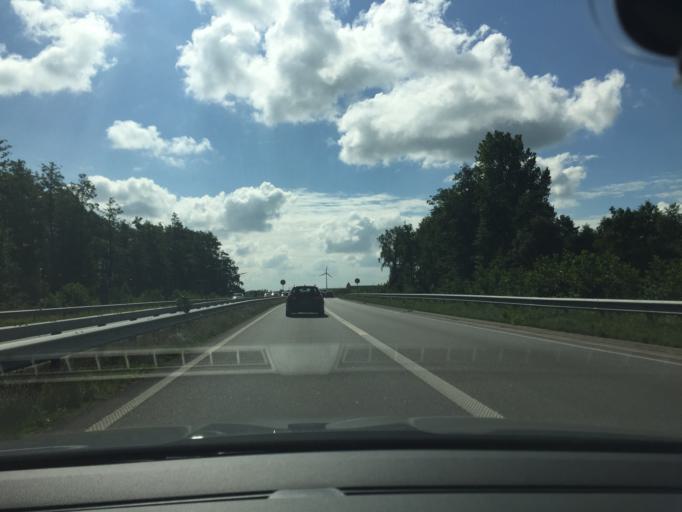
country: DE
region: Lower Saxony
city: Schortens
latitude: 53.5419
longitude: 7.9720
